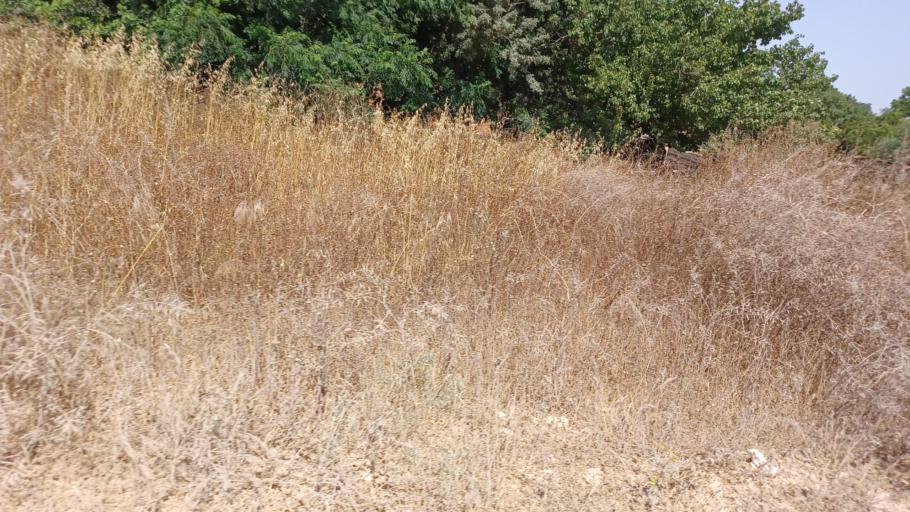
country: CY
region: Ammochostos
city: Frenaros
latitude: 35.0151
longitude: 33.9502
